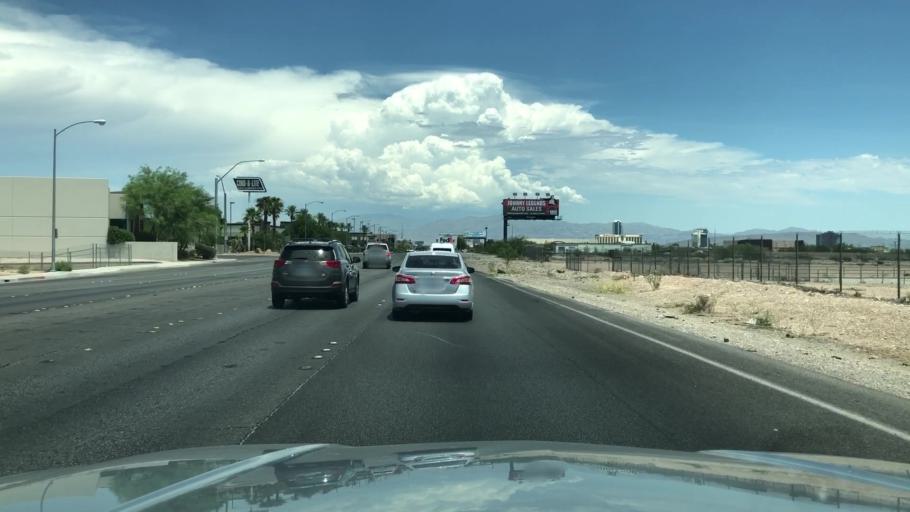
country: US
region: Nevada
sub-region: Clark County
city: Spring Valley
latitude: 36.0780
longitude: -115.2078
